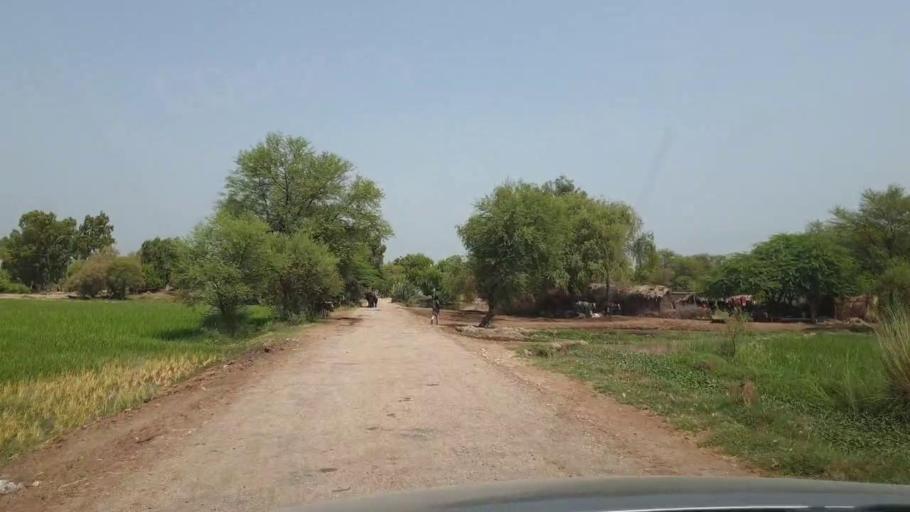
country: PK
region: Sindh
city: Madeji
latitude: 27.8073
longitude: 68.5204
